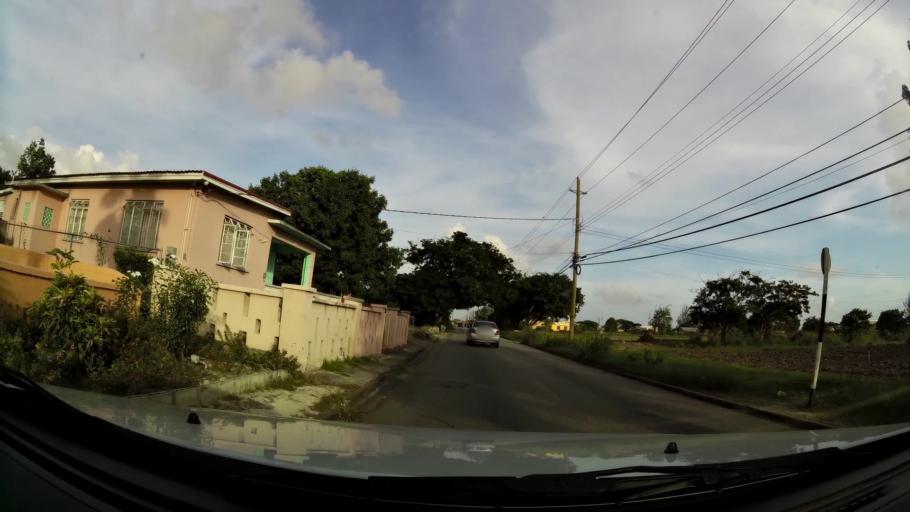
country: BB
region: Christ Church
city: Oistins
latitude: 13.0582
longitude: -59.5237
